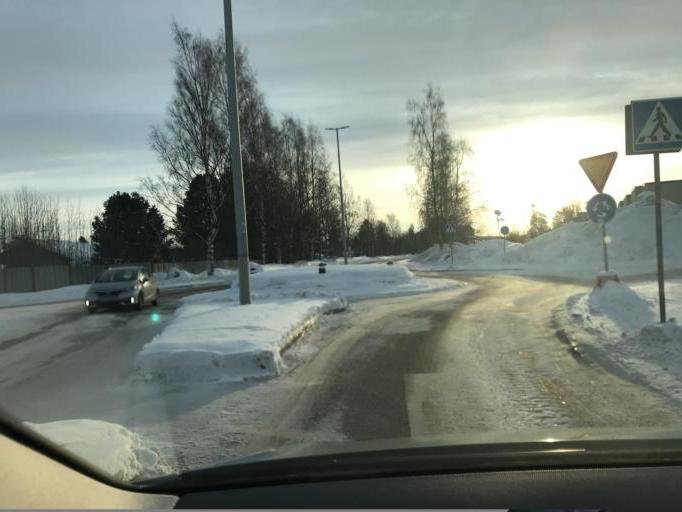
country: SE
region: Norrbotten
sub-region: Lulea Kommun
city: Bergnaset
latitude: 65.6040
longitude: 22.1197
